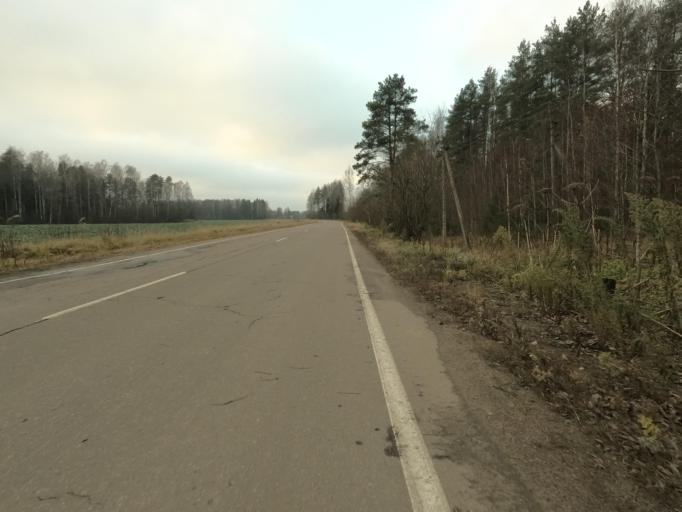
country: RU
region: Leningrad
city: Kirovsk
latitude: 59.8000
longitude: 30.9988
